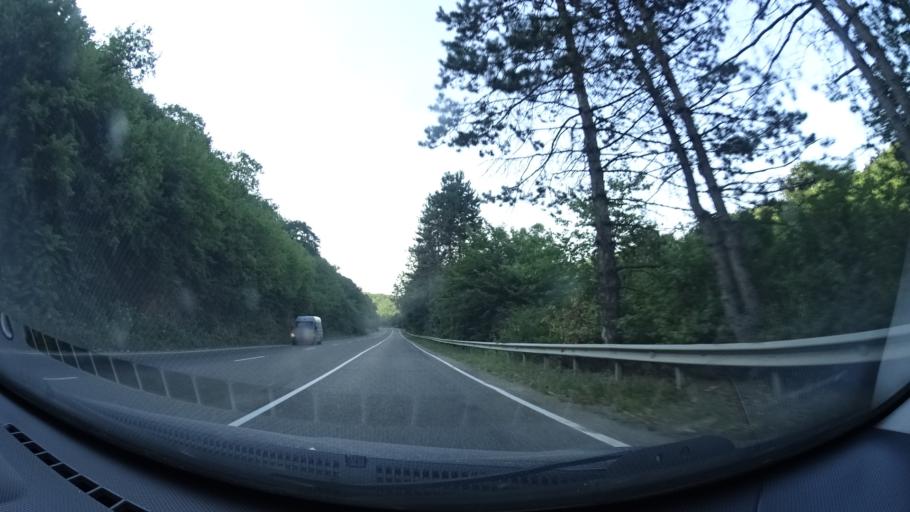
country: GE
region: Kakheti
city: Sighnaghi
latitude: 41.6522
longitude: 45.8341
